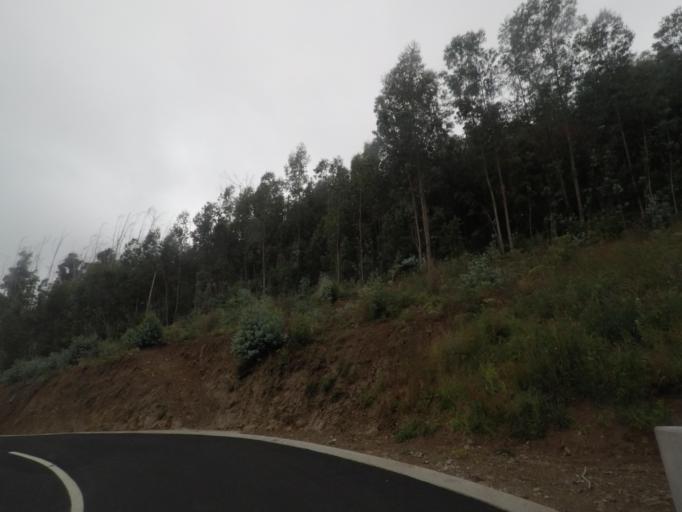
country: PT
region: Madeira
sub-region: Calheta
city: Arco da Calheta
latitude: 32.7491
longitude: -17.1543
